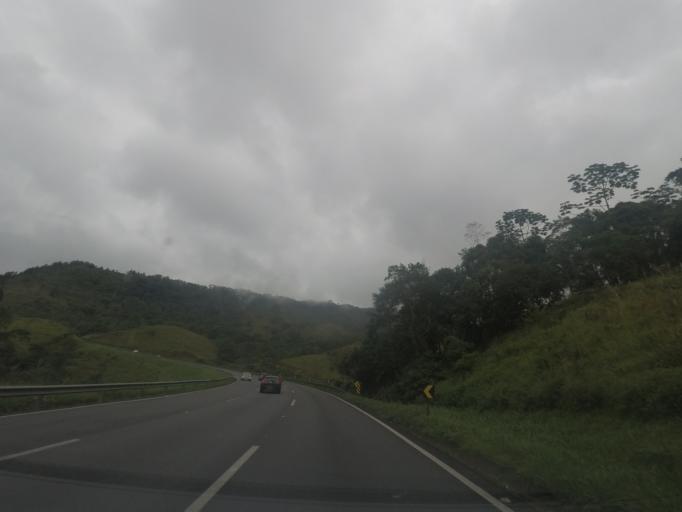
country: BR
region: Sao Paulo
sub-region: Cajati
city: Cajati
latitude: -24.8788
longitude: -48.2291
